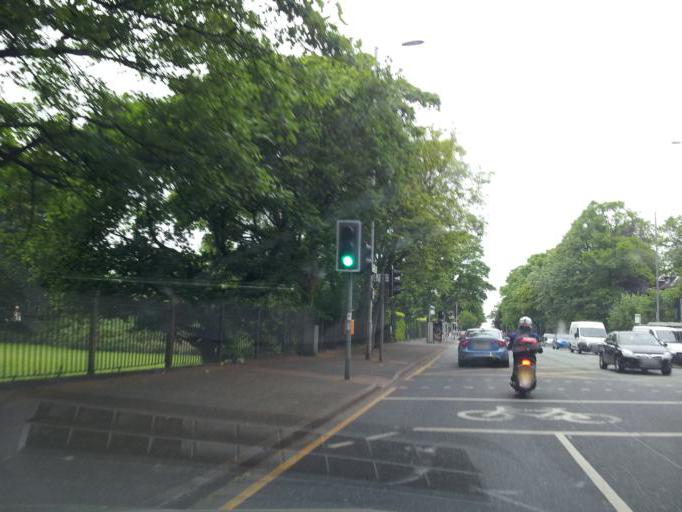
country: GB
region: England
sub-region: Manchester
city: Crumpsall
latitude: 53.5181
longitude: -2.2488
